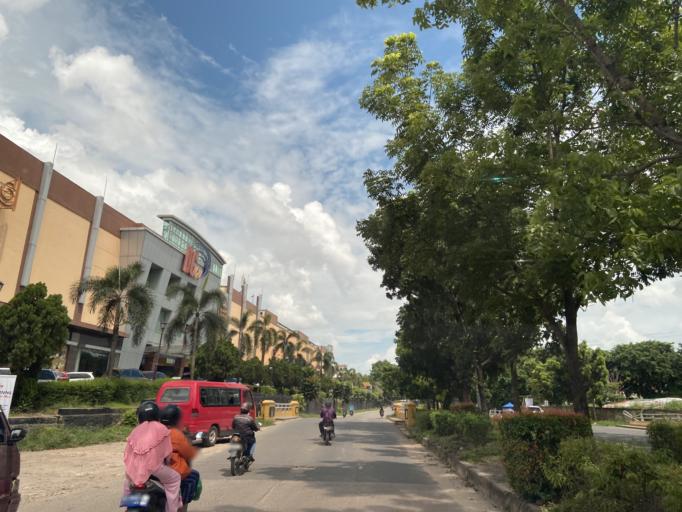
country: SG
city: Singapore
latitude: 1.1422
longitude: 104.0031
